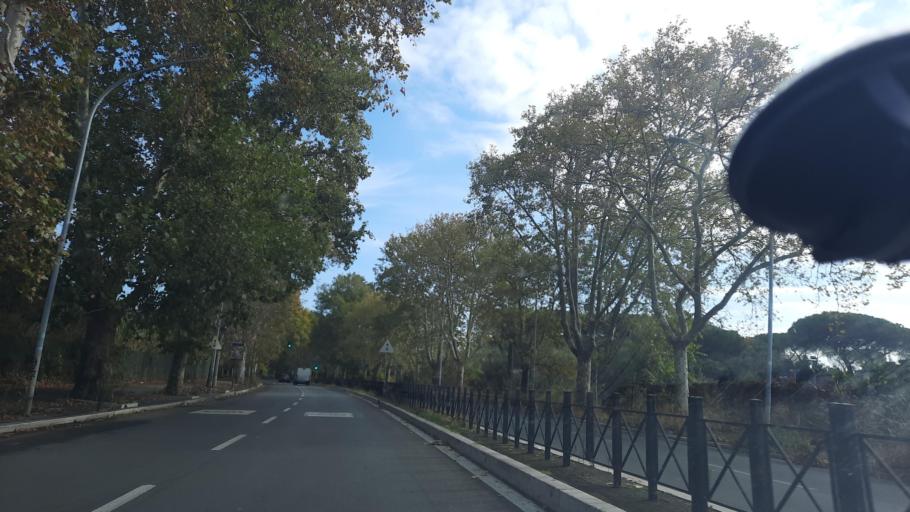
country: VA
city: Vatican City
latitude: 41.8592
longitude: 12.4727
